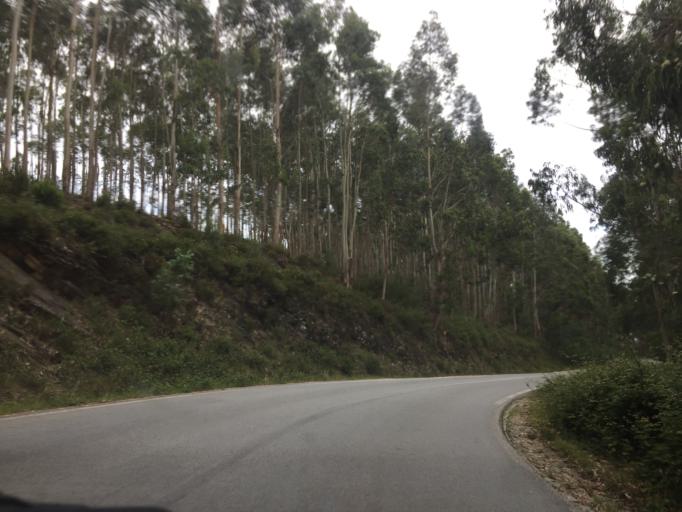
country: PT
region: Aveiro
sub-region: Agueda
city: Aguada de Cima
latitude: 40.4918
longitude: -8.3324
